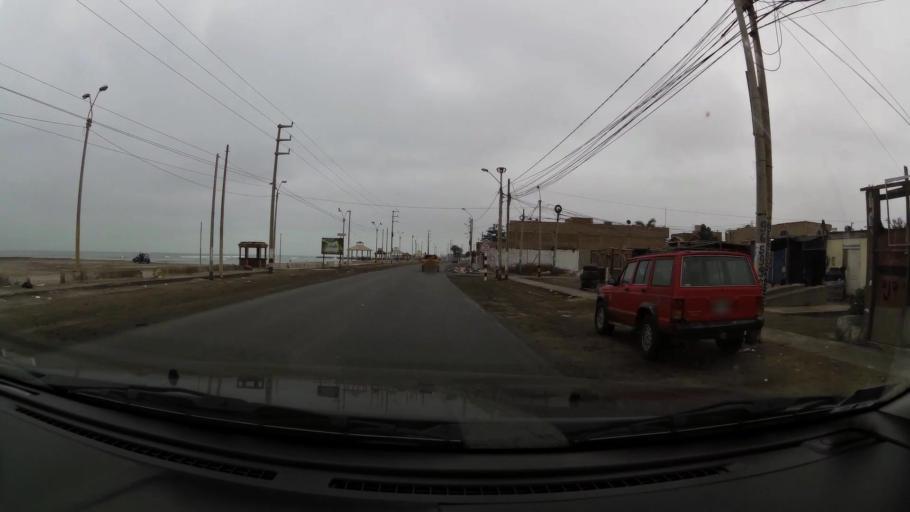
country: PE
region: Ica
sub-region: Provincia de Pisco
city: Pisco
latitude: -13.7381
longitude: -76.2258
